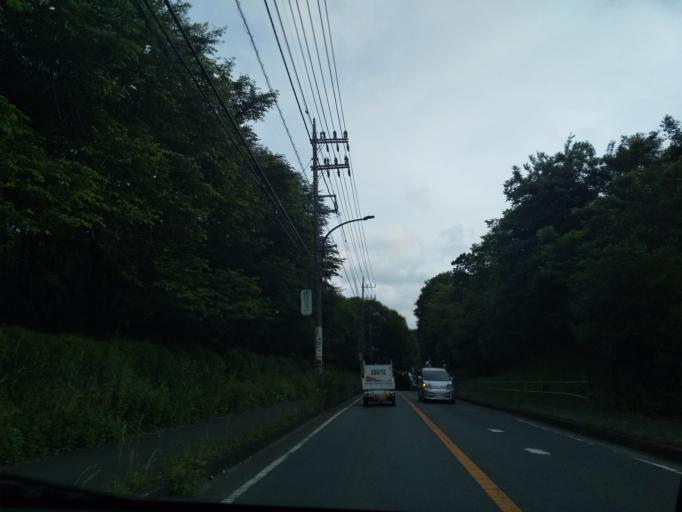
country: JP
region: Kanagawa
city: Zama
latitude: 35.5167
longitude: 139.3932
